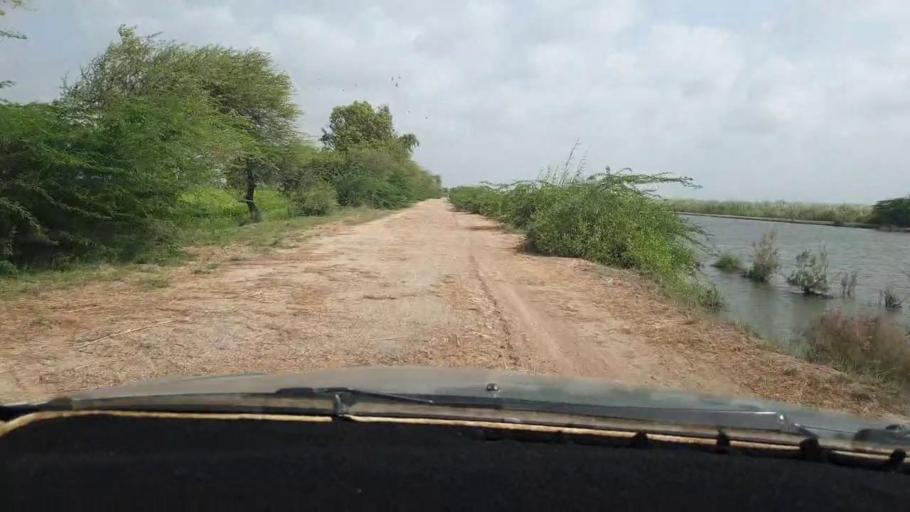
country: PK
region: Sindh
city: Tando Bago
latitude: 24.7786
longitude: 69.0262
